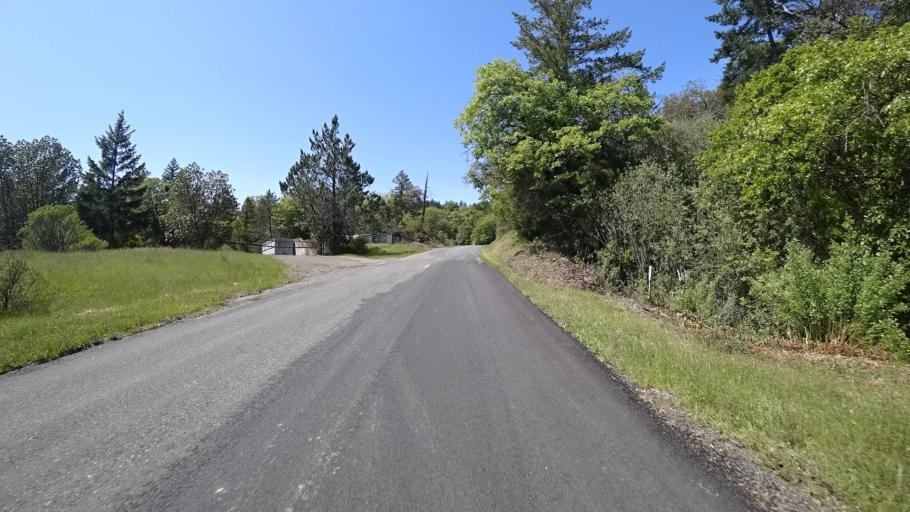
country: US
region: California
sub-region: Humboldt County
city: Redway
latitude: 40.2735
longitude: -123.6290
